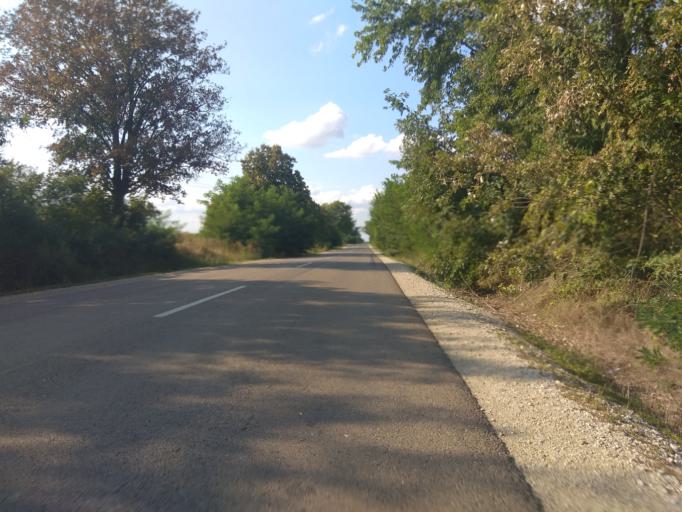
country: HU
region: Borsod-Abauj-Zemplen
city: Hejobaba
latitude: 47.8965
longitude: 20.8923
